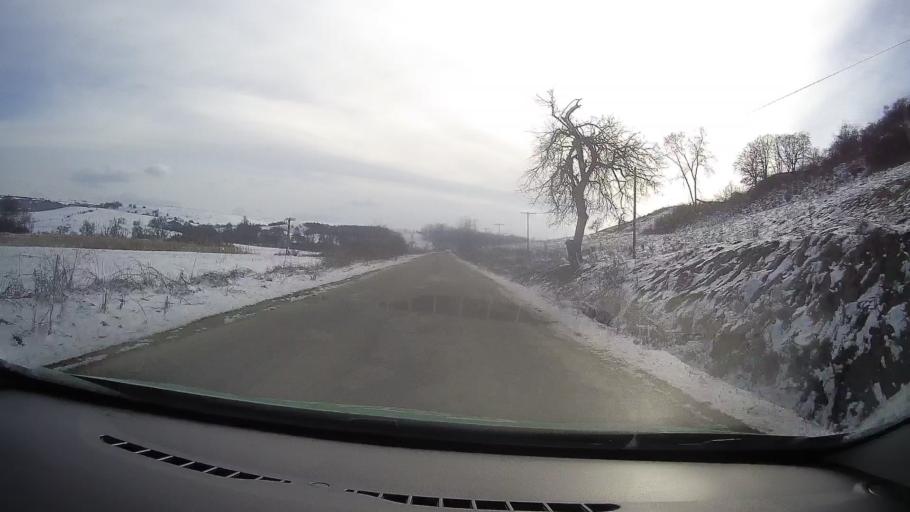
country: RO
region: Sibiu
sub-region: Comuna Iacobeni
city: Iacobeni
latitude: 46.0188
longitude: 24.6961
